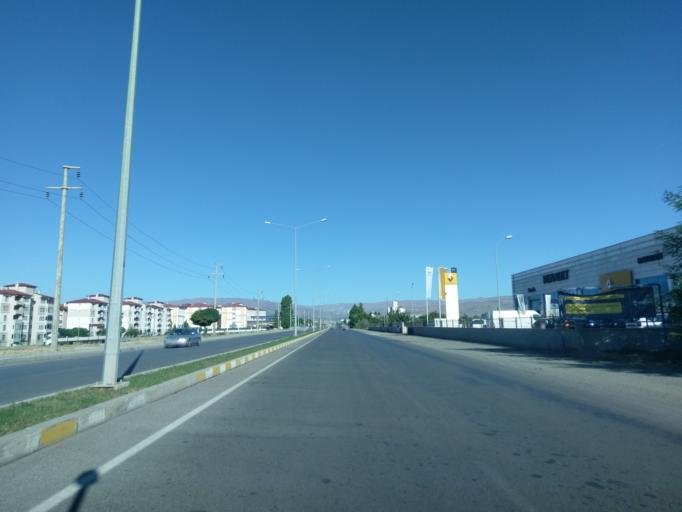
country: TR
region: Erzincan
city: Erzincan
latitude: 39.7571
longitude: 39.4477
